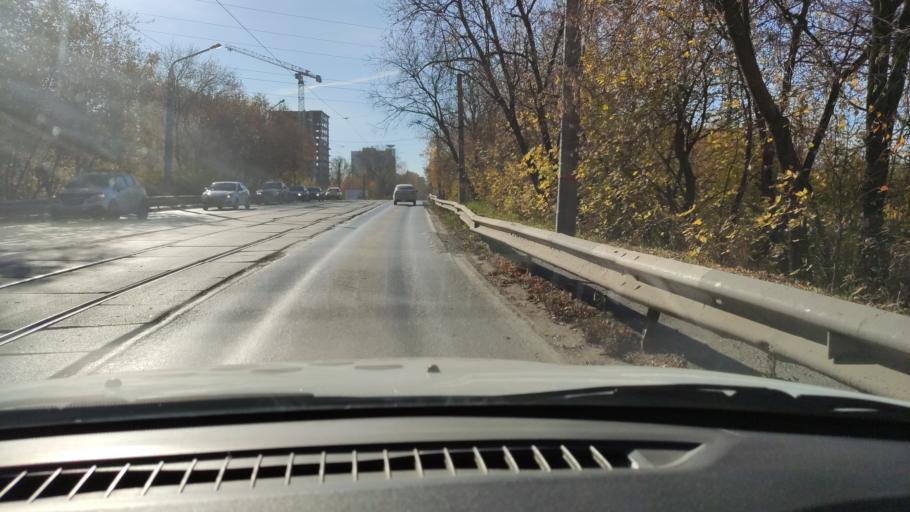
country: RU
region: Perm
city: Perm
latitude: 57.9933
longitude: 56.2182
